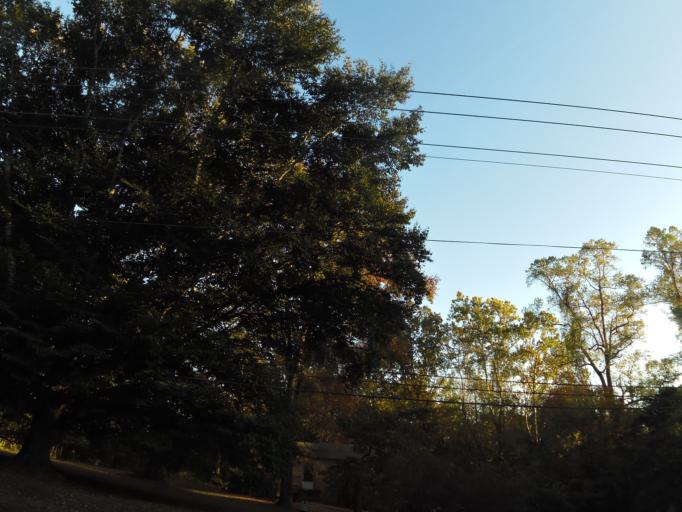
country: US
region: Tennessee
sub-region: Knox County
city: Farragut
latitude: 35.9804
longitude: -84.0718
